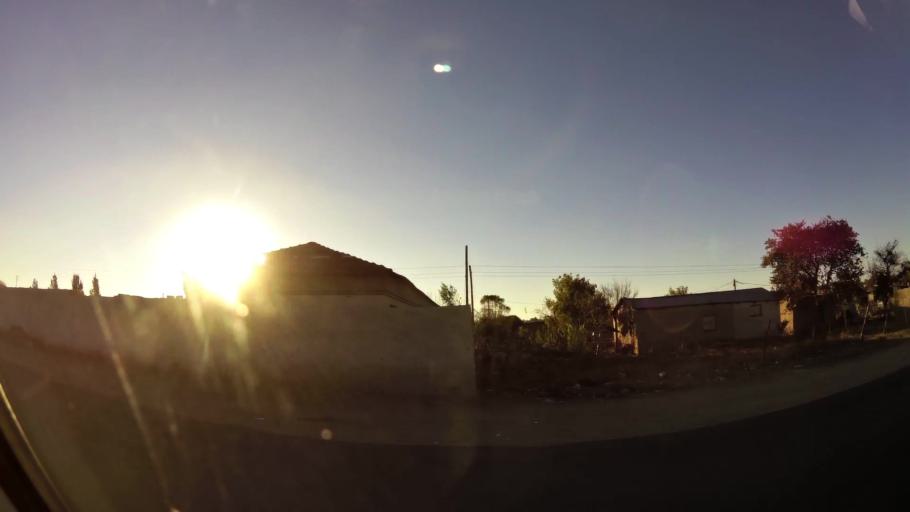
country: ZA
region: Limpopo
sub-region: Capricorn District Municipality
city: Polokwane
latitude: -23.8301
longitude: 29.3743
